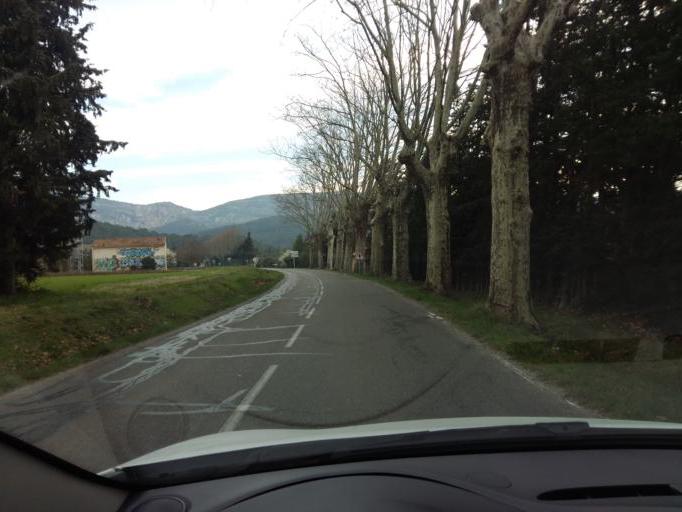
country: FR
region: Provence-Alpes-Cote d'Azur
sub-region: Departement du Vaucluse
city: Lagnes
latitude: 43.9171
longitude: 5.1030
